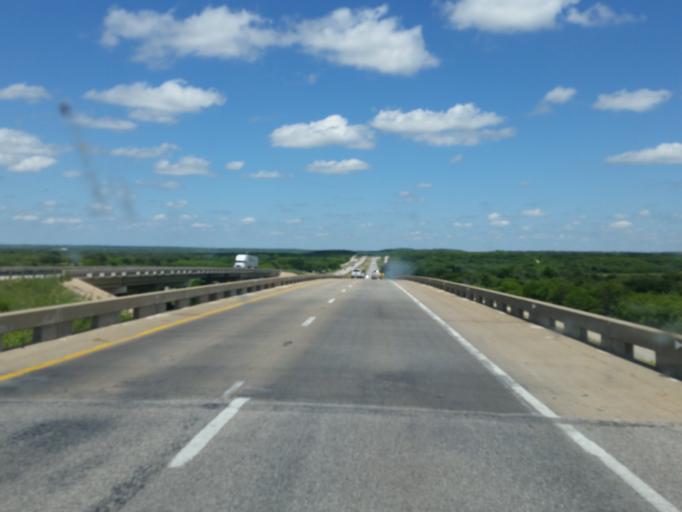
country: US
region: Texas
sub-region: Eastland County
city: Cisco
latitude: 32.3766
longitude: -99.1663
